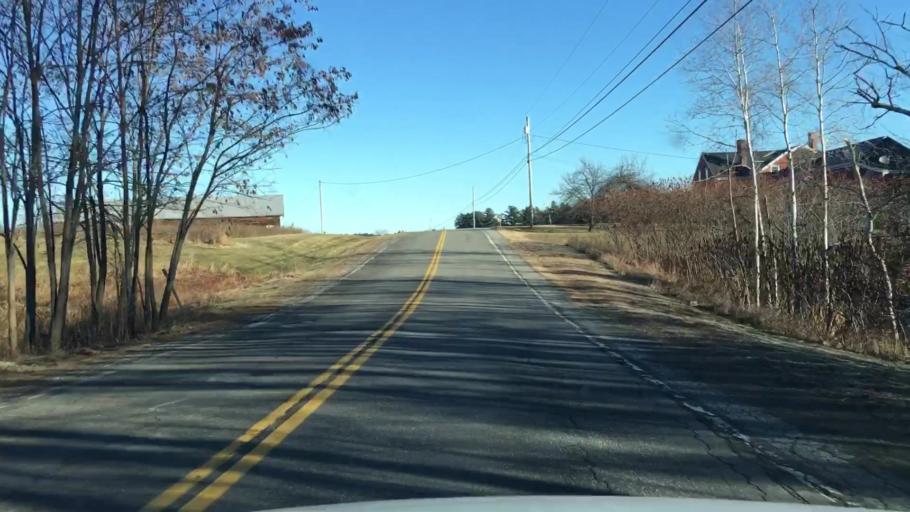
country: US
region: Maine
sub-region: Somerset County
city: Fairfield
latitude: 44.5590
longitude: -69.5811
